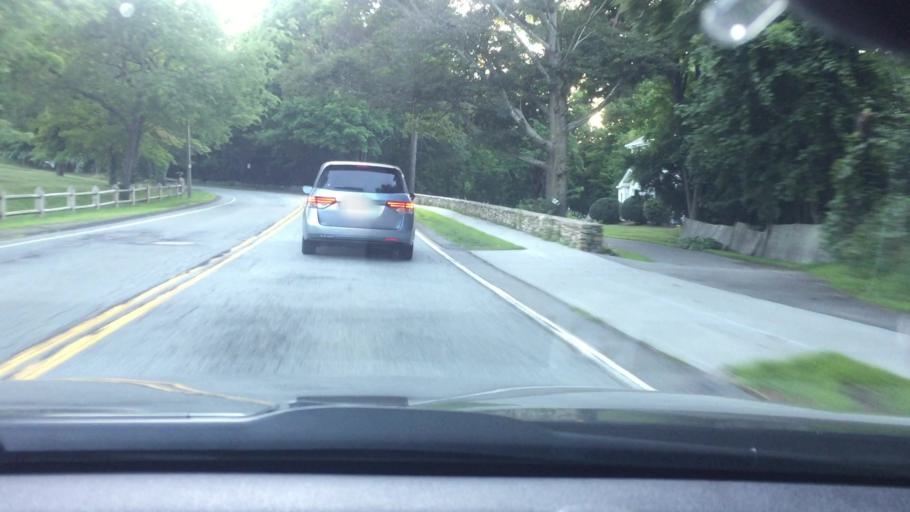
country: US
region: Massachusetts
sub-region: Suffolk County
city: Jamaica Plain
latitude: 42.3150
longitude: -71.1356
